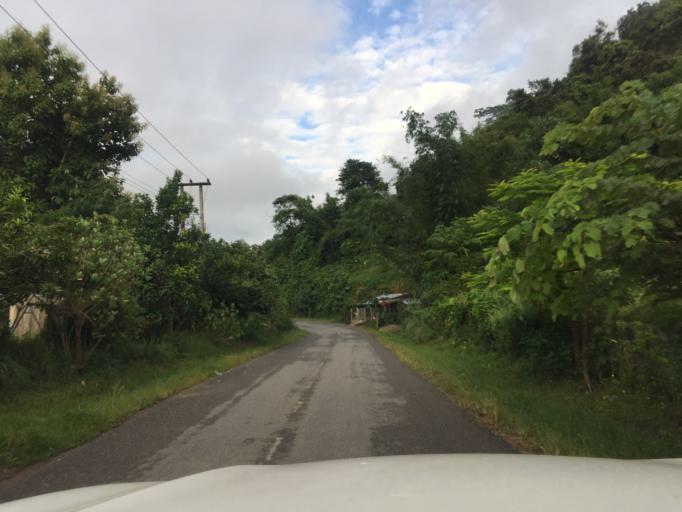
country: LA
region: Phongsali
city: Khoa
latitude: 21.1024
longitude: 102.2650
